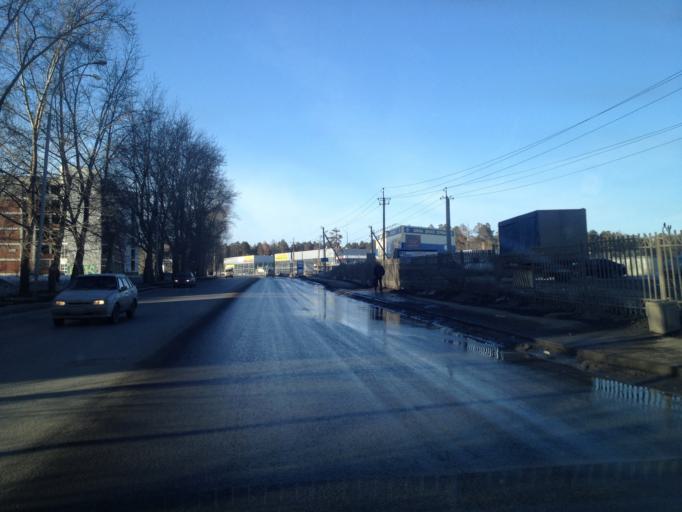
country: RU
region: Sverdlovsk
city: Yekaterinburg
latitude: 56.9095
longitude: 60.6198
